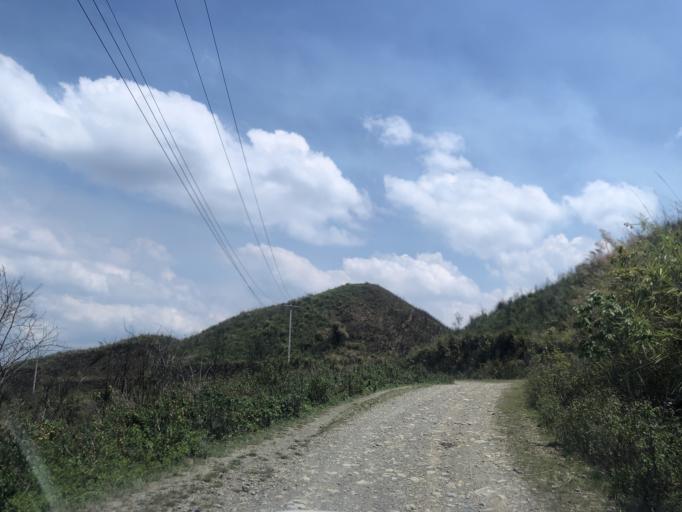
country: LA
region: Phongsali
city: Phongsali
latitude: 21.4130
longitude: 102.1865
